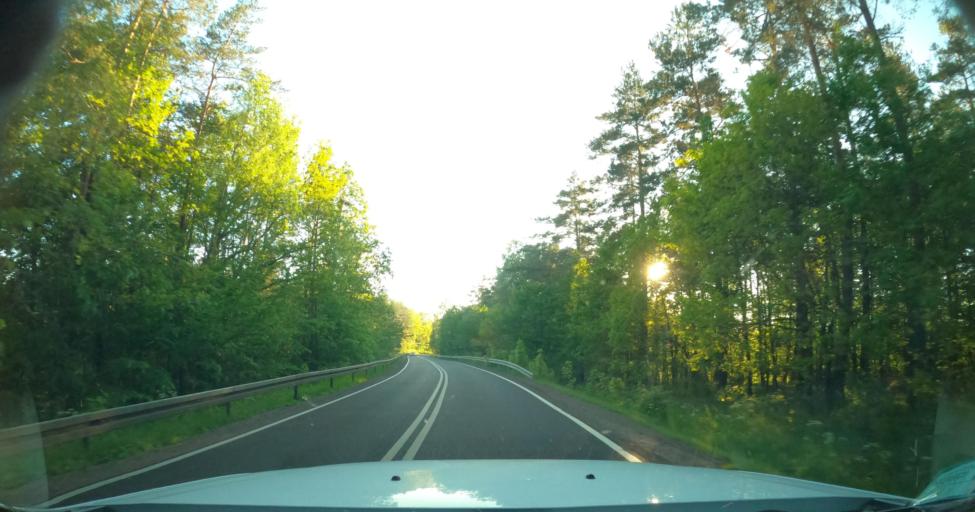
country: PL
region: Pomeranian Voivodeship
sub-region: Powiat bytowski
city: Czarna Dabrowka
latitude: 54.3393
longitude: 17.6330
